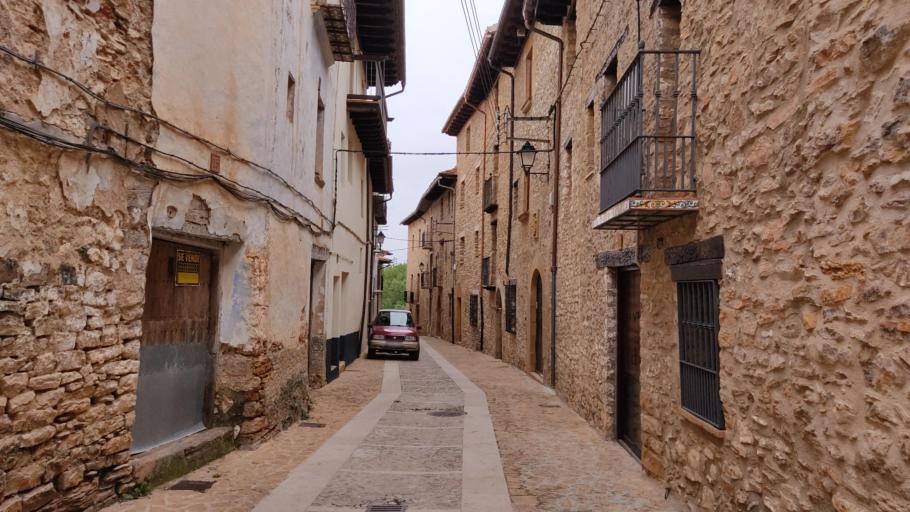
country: ES
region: Aragon
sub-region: Provincia de Teruel
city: La Iglesuela del Cid
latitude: 40.4815
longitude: -0.3183
